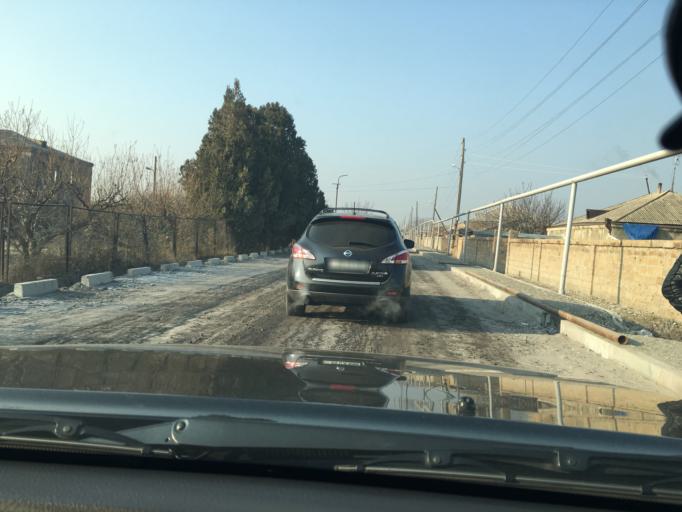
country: AM
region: Armavir
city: Janfida
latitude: 40.0428
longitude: 44.0242
